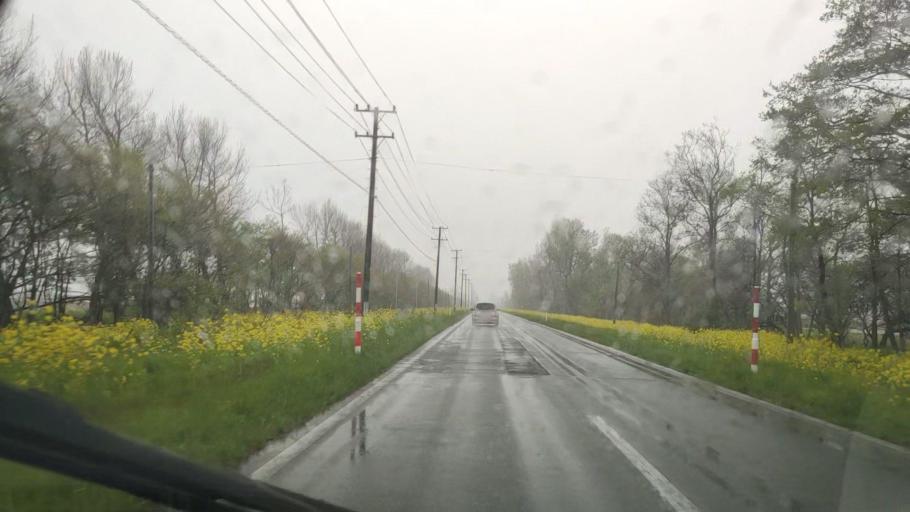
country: JP
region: Akita
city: Tenno
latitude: 39.9874
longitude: 139.9463
